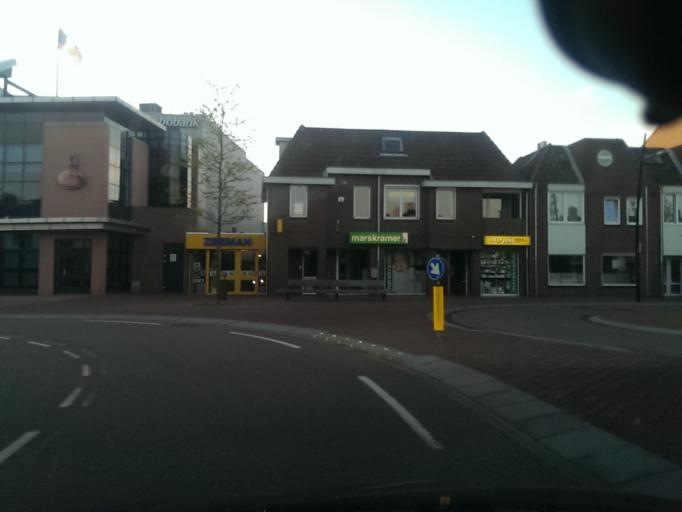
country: NL
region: Limburg
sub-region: Gemeente Nederweert
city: Nederweert
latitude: 51.2825
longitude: 5.7486
